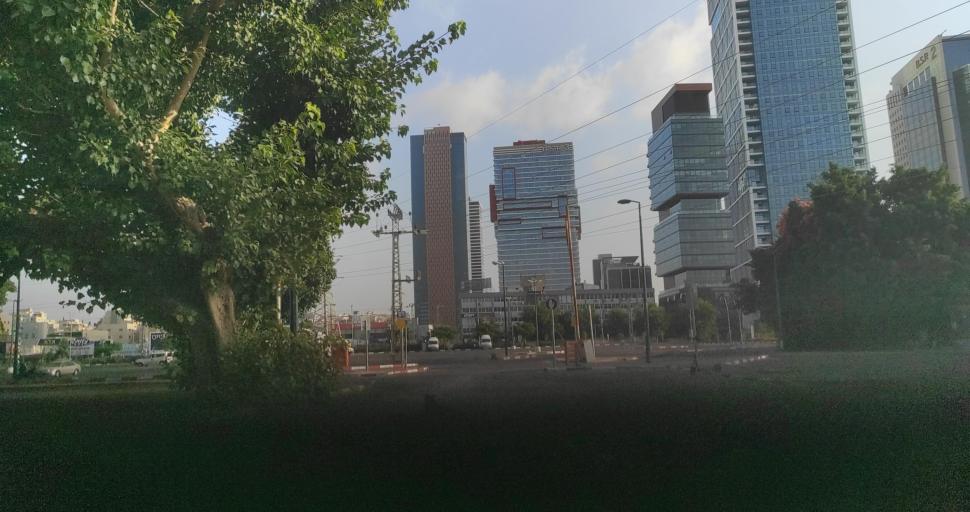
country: IL
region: Tel Aviv
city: Ramat Gan
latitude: 32.0991
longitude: 34.8233
